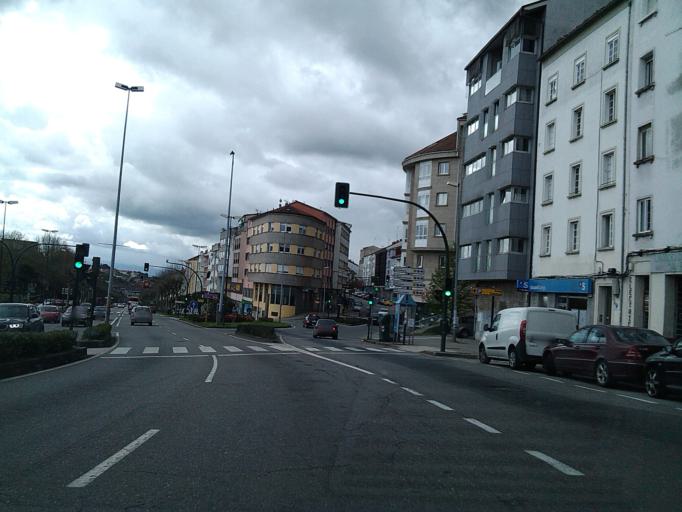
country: ES
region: Galicia
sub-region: Provincia da Coruna
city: Santiago de Compostela
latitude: 42.8850
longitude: -8.5337
